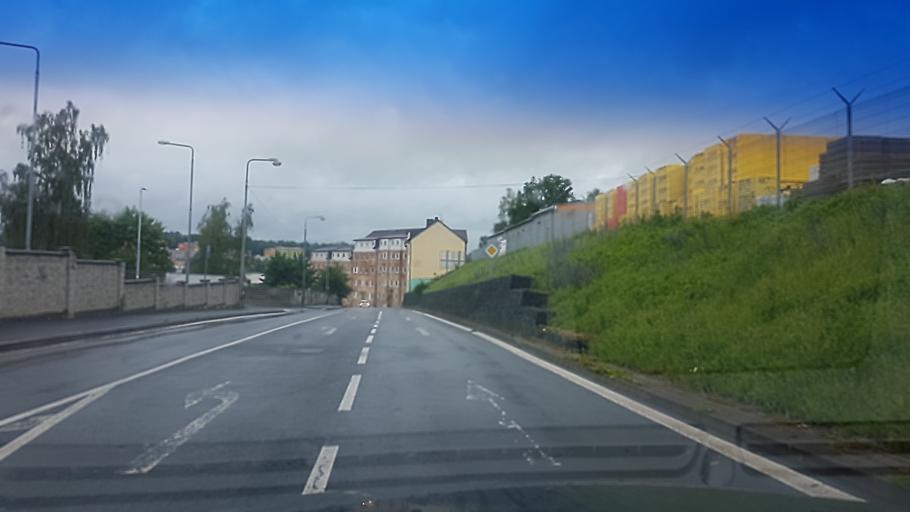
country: CZ
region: Karlovarsky
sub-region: Okres Cheb
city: Cheb
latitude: 50.0789
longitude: 12.3813
